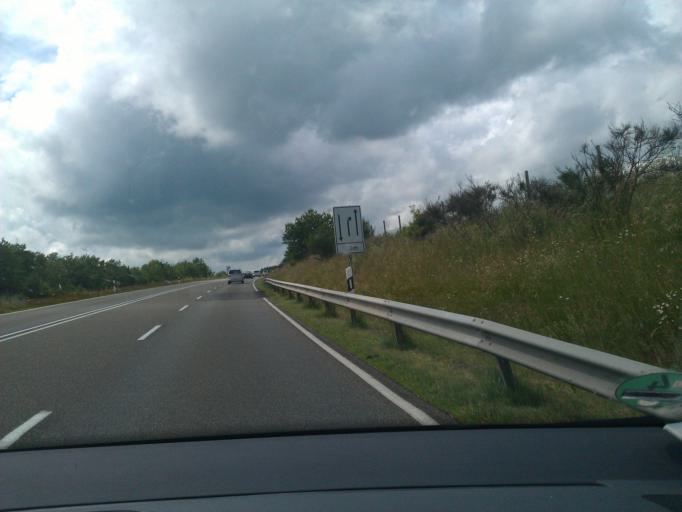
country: DE
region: Rheinland-Pfalz
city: Habscheid
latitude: 50.1983
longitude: 6.2661
